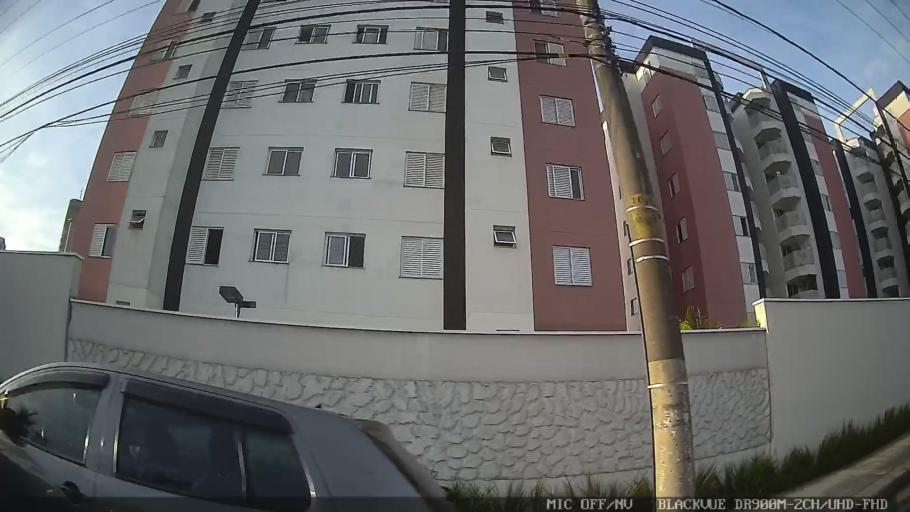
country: BR
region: Sao Paulo
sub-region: Mogi das Cruzes
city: Mogi das Cruzes
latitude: -23.5155
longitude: -46.1689
